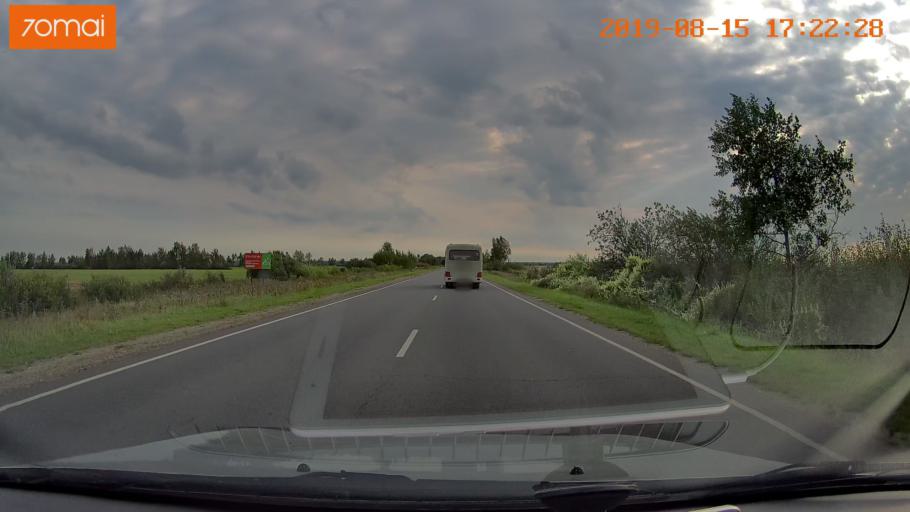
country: RU
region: Moskovskaya
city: Ashitkovo
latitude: 55.4141
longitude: 38.5621
